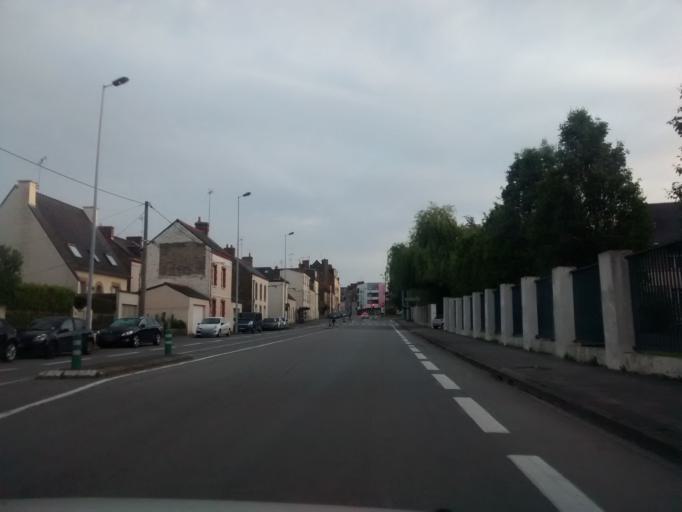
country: FR
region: Brittany
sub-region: Departement d'Ille-et-Vilaine
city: Rennes
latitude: 48.1126
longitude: -1.6563
